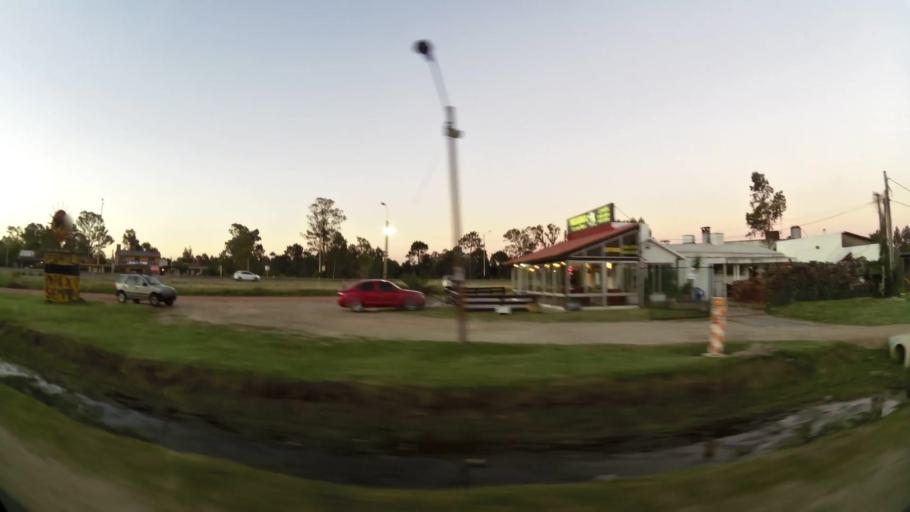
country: UY
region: Canelones
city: Colonia Nicolich
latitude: -34.8203
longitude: -55.9539
